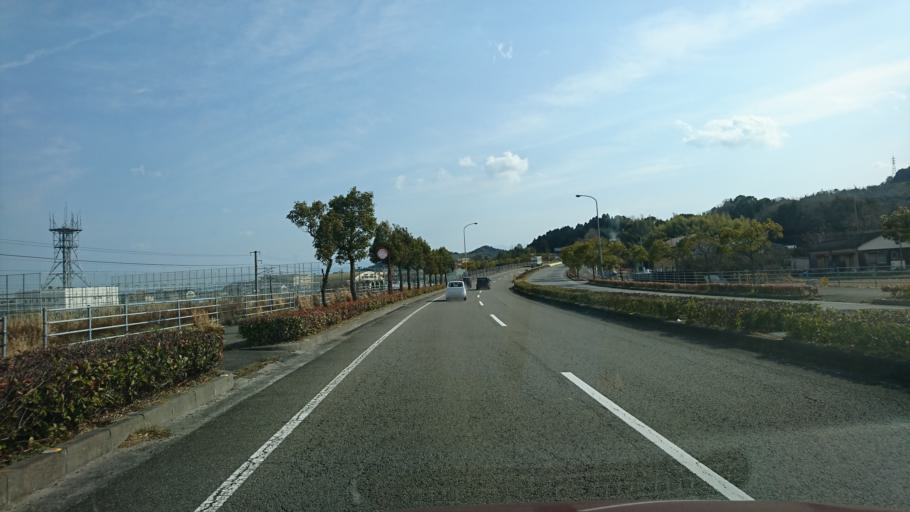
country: JP
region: Ehime
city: Saijo
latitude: 34.0184
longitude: 133.0298
